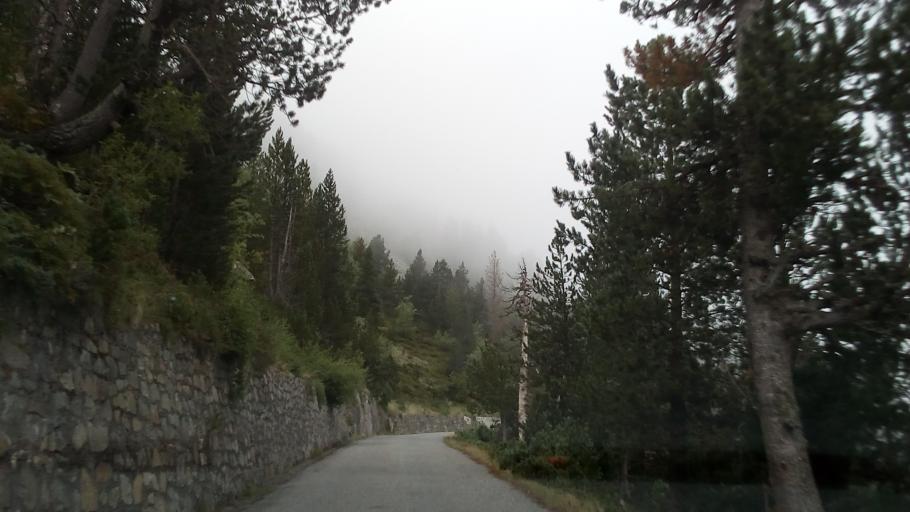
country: FR
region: Midi-Pyrenees
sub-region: Departement des Hautes-Pyrenees
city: Saint-Lary-Soulan
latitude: 42.8208
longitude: 0.1604
